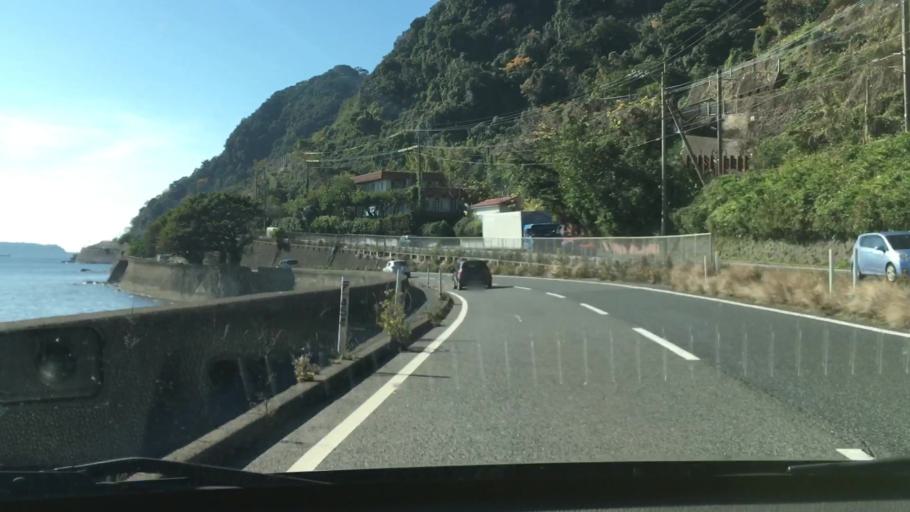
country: JP
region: Kagoshima
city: Kagoshima-shi
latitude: 31.6454
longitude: 130.6034
